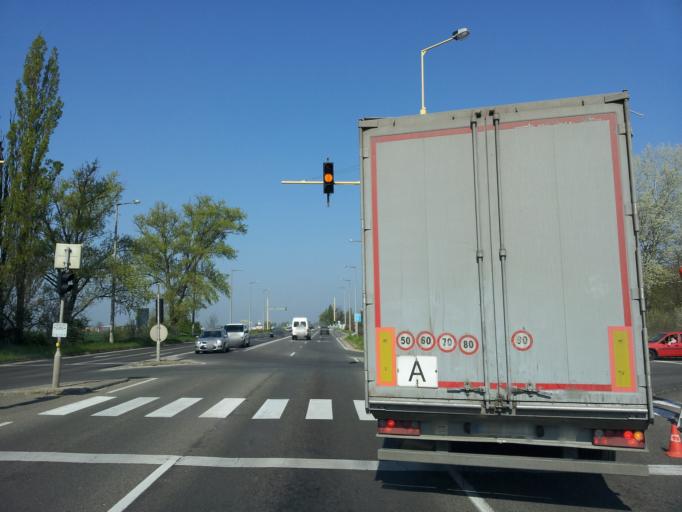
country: HU
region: Fejer
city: Szekesfehervar
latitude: 47.1799
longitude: 18.4745
